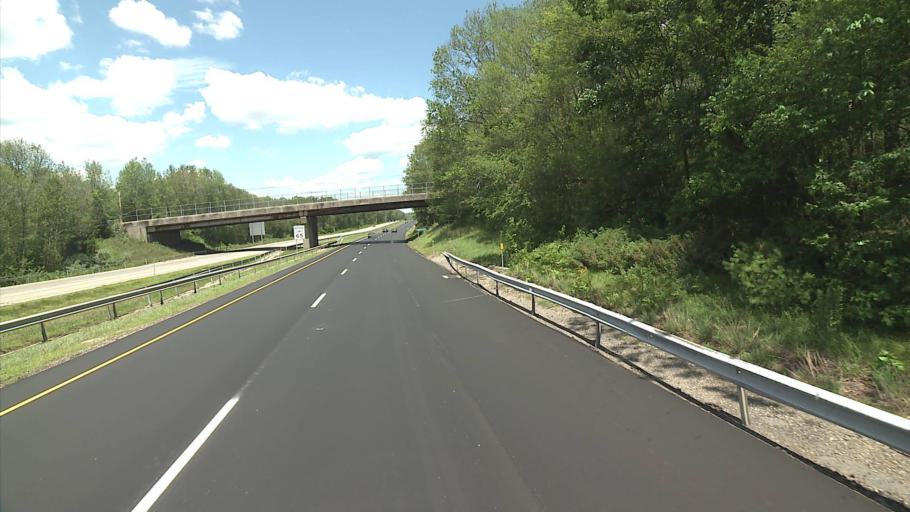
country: US
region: Connecticut
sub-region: Windham County
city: Danielson
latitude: 41.7692
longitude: -71.8721
